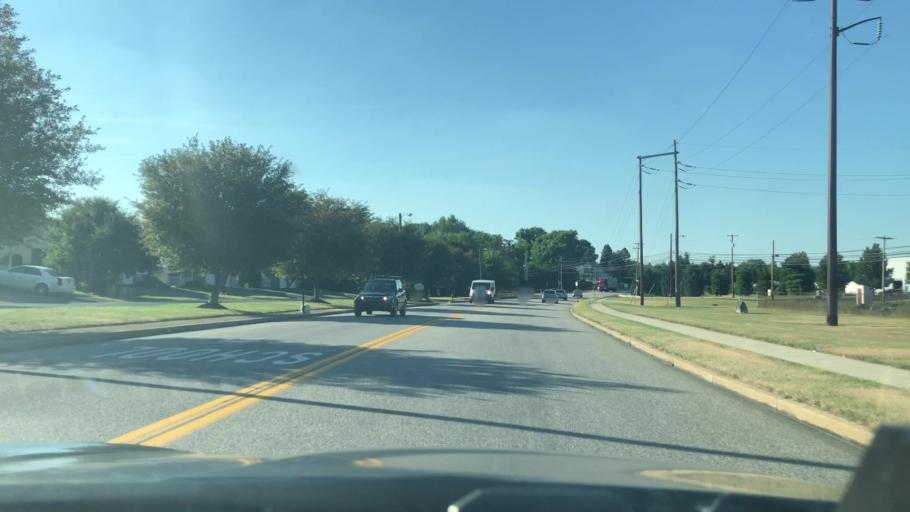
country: US
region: Pennsylvania
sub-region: Cumberland County
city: Mechanicsburg
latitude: 40.2219
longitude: -77.0071
